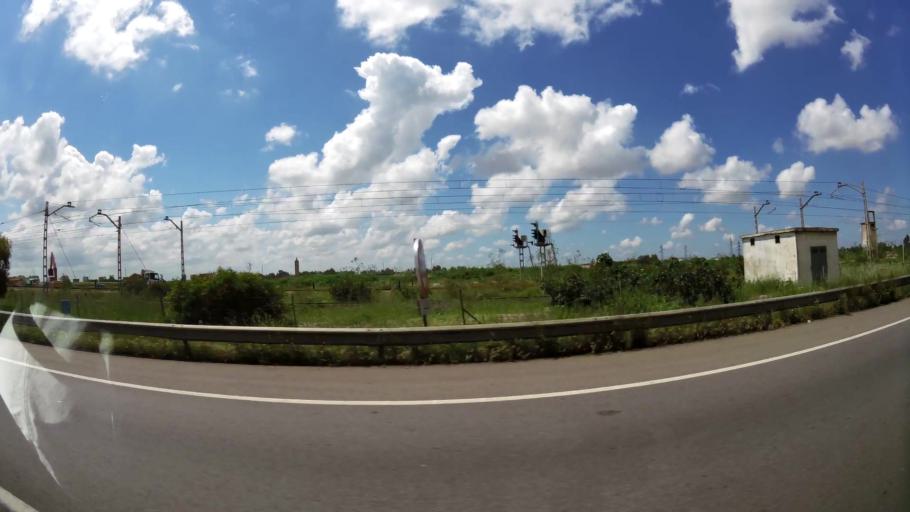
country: MA
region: Chaouia-Ouardigha
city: Nouaseur
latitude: 33.4168
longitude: -7.6268
